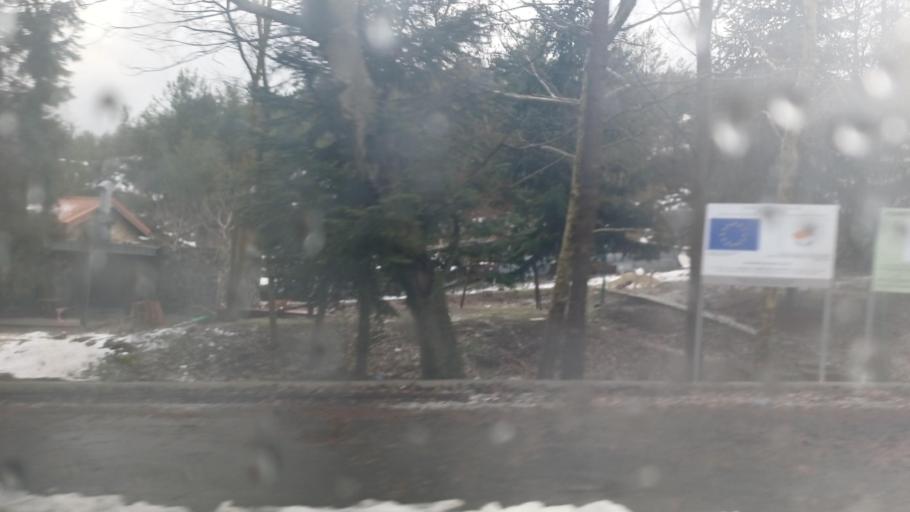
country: CY
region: Limassol
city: Kyperounta
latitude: 34.9405
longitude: 32.9639
